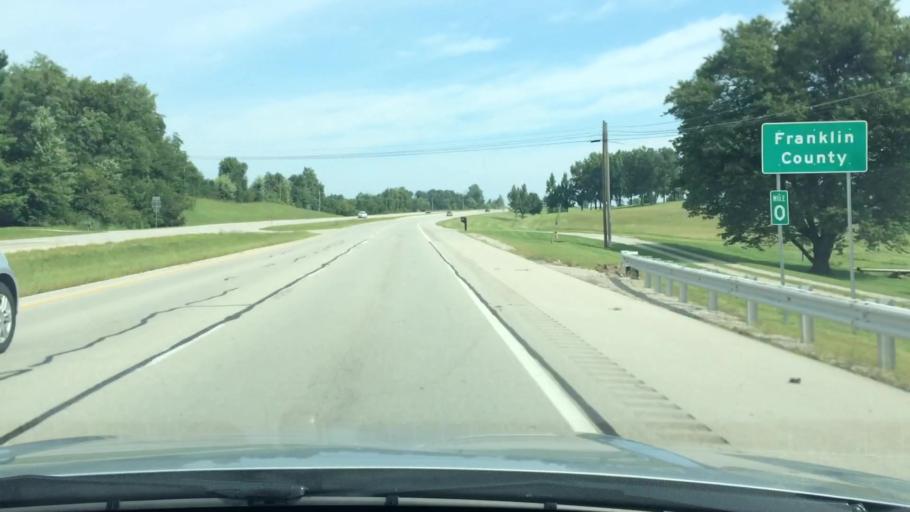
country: US
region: Kentucky
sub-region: Anderson County
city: Lawrenceburg
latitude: 38.0998
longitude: -84.9187
